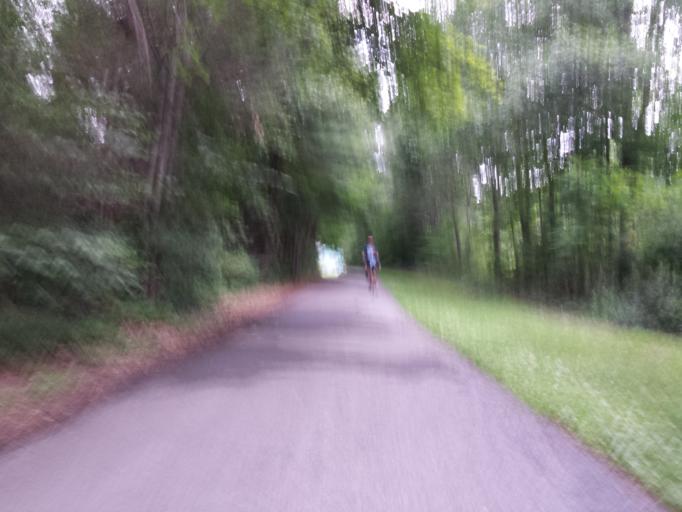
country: US
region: New York
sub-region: Ulster County
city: Highland
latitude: 41.7323
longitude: -73.9732
